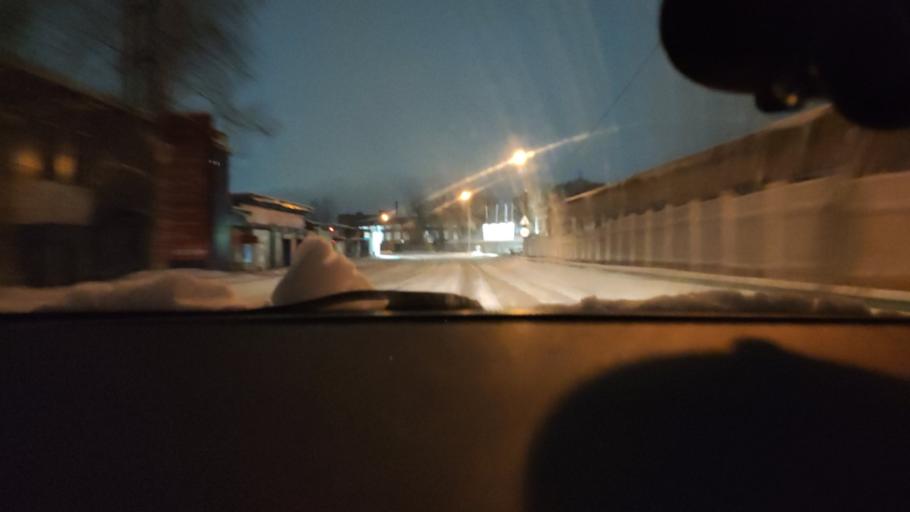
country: RU
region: Perm
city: Krasnokamsk
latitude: 58.0698
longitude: 55.7916
